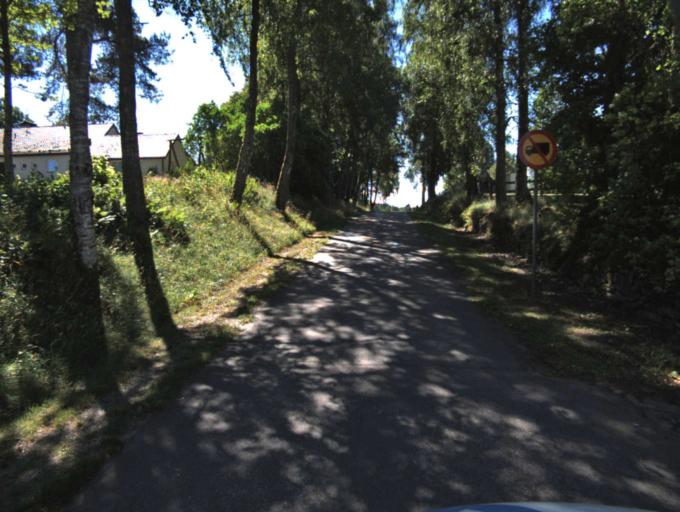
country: SE
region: Vaestra Goetaland
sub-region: Ulricehamns Kommun
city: Ulricehamn
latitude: 57.6627
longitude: 13.4306
